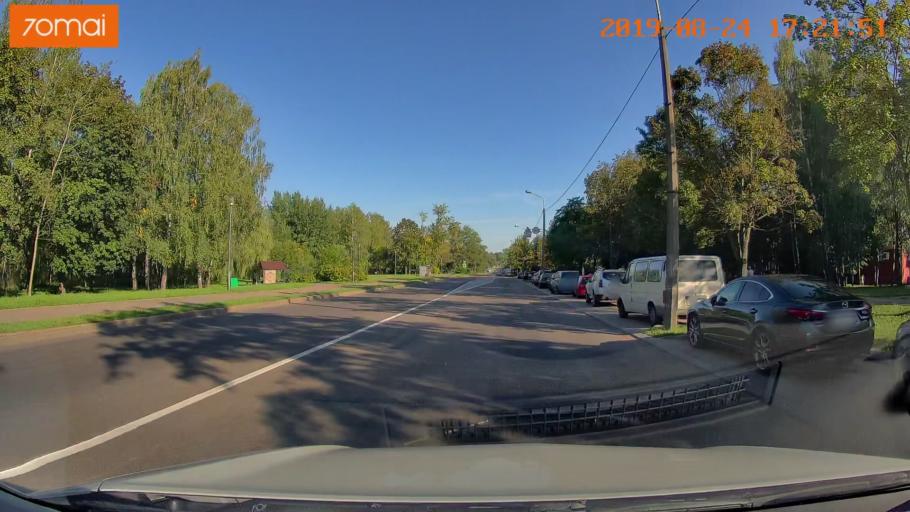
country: BY
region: Minsk
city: Hatava
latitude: 53.8484
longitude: 27.6387
